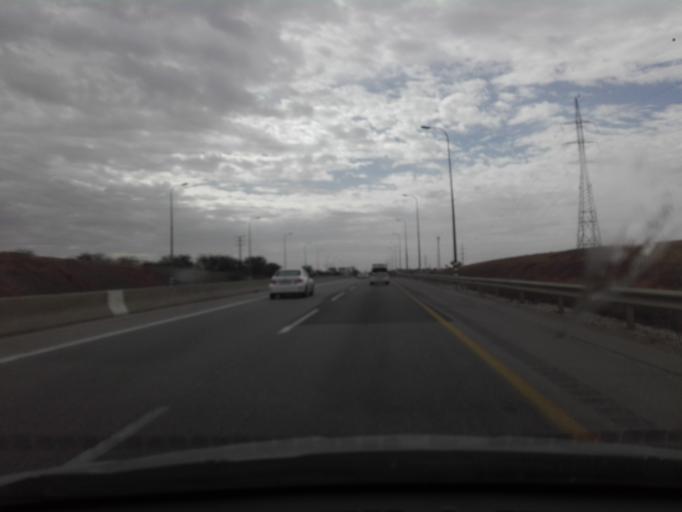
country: IL
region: Southern District
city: Lehavim
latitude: 31.3570
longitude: 34.7944
